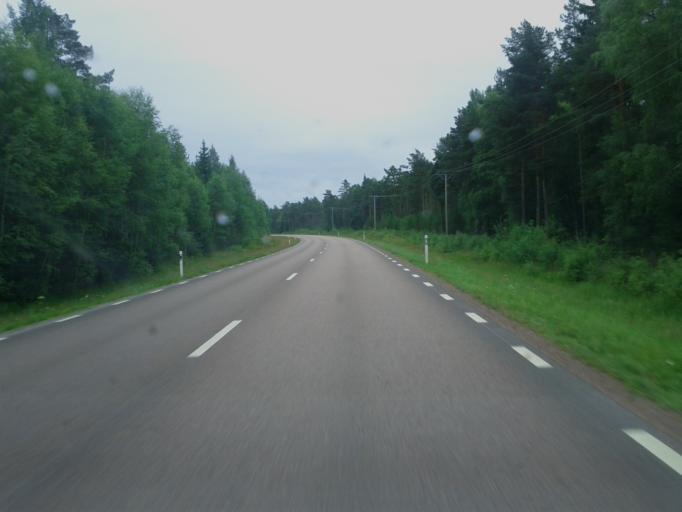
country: SE
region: Dalarna
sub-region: Mora Kommun
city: Mora
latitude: 61.0370
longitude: 14.5093
